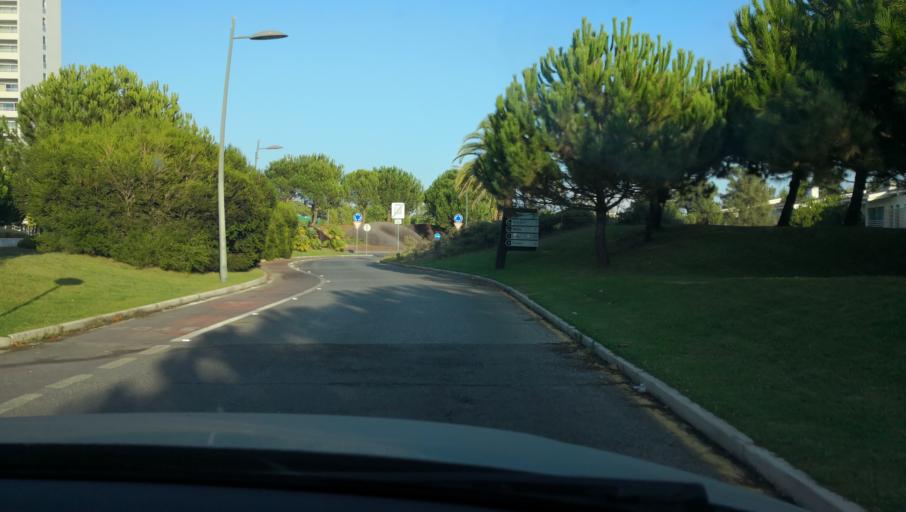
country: PT
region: Setubal
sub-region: Setubal
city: Setubal
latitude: 38.4895
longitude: -8.9020
